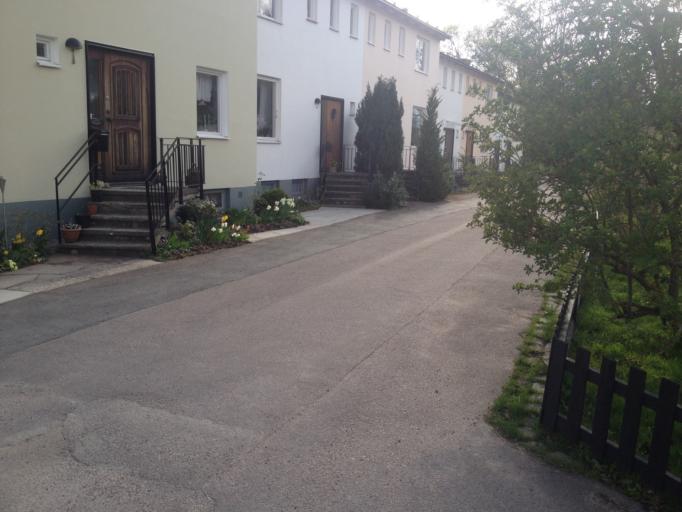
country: SE
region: Kalmar
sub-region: Kalmar Kommun
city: Kalmar
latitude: 56.6823
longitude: 16.3471
